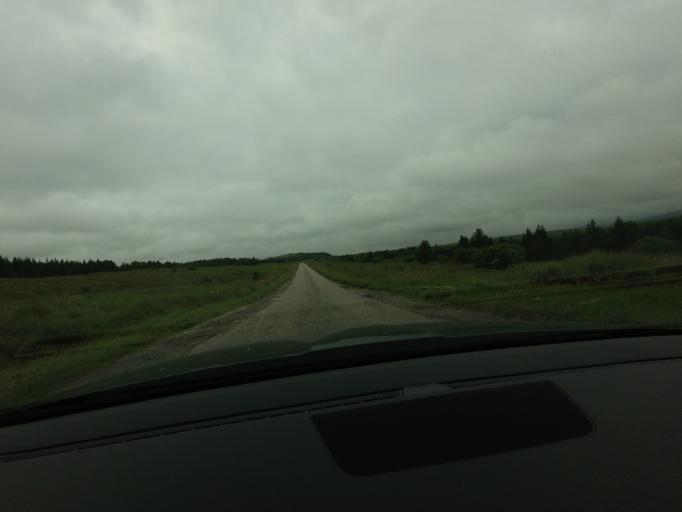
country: GB
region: Scotland
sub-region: Highland
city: Alness
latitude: 58.1217
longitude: -4.4483
